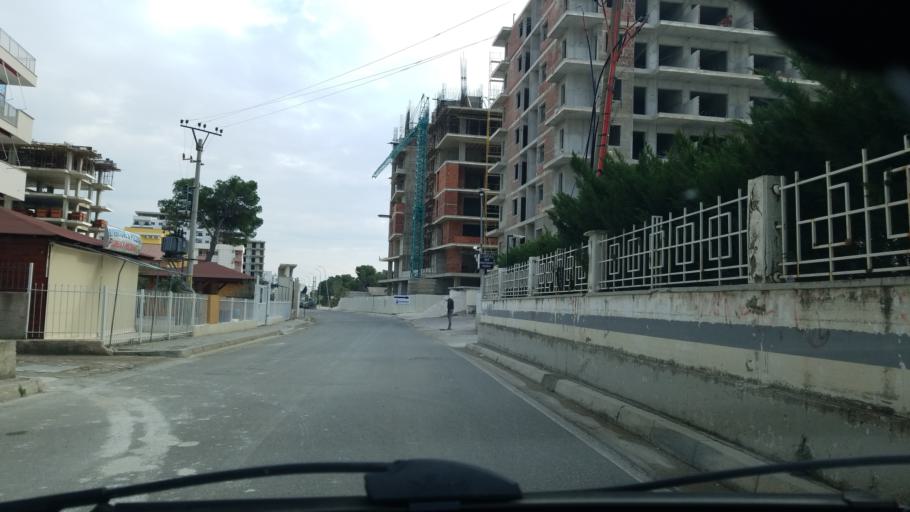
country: AL
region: Lezhe
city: Shengjin
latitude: 41.8067
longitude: 19.5995
